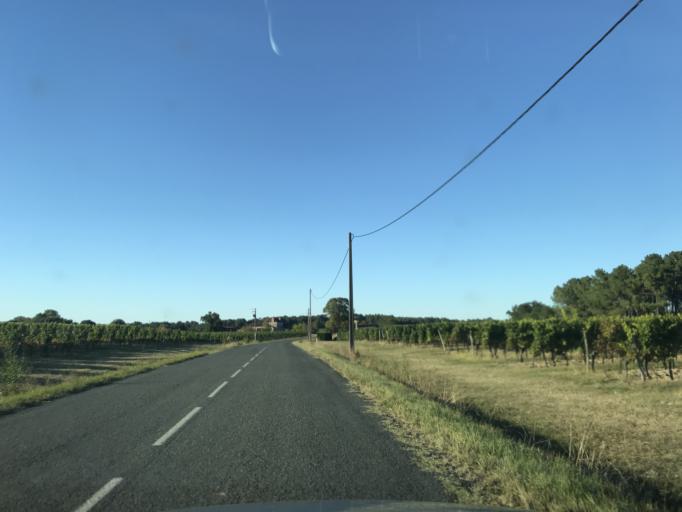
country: FR
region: Aquitaine
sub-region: Departement de la Gironde
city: Sauveterre-de-Guyenne
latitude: 44.7164
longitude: -0.0650
